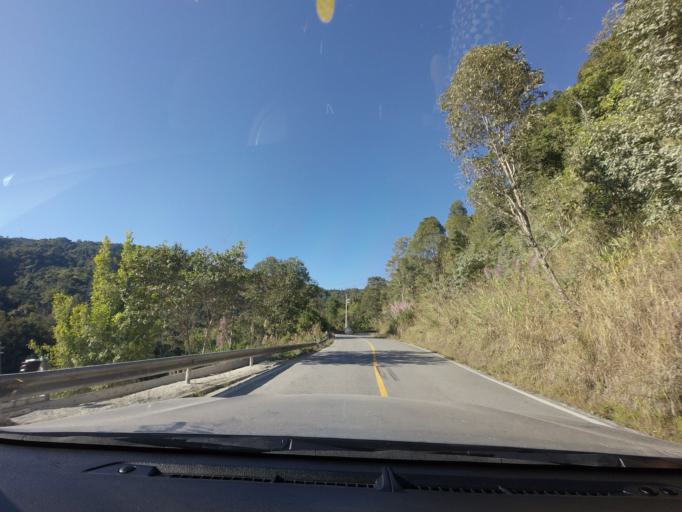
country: TH
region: Mae Hong Son
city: Mae Hi
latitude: 19.2210
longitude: 98.6721
